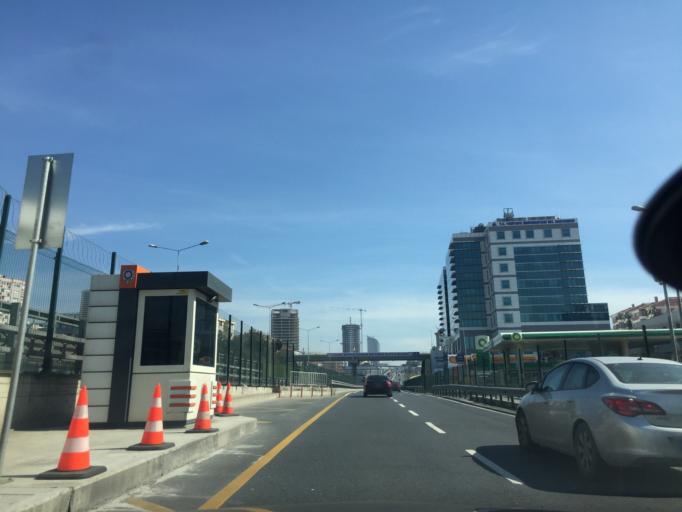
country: TR
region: Istanbul
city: UEskuedar
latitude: 41.0048
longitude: 29.0291
